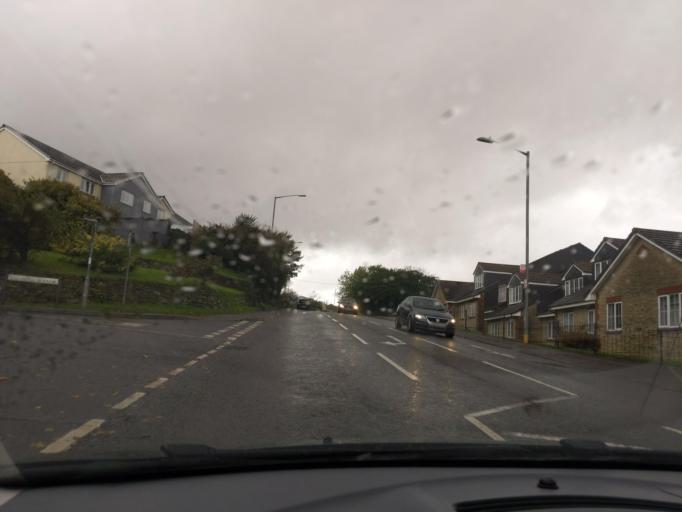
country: GB
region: England
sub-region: Cornwall
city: Wadebridge
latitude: 50.5177
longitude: -4.8470
